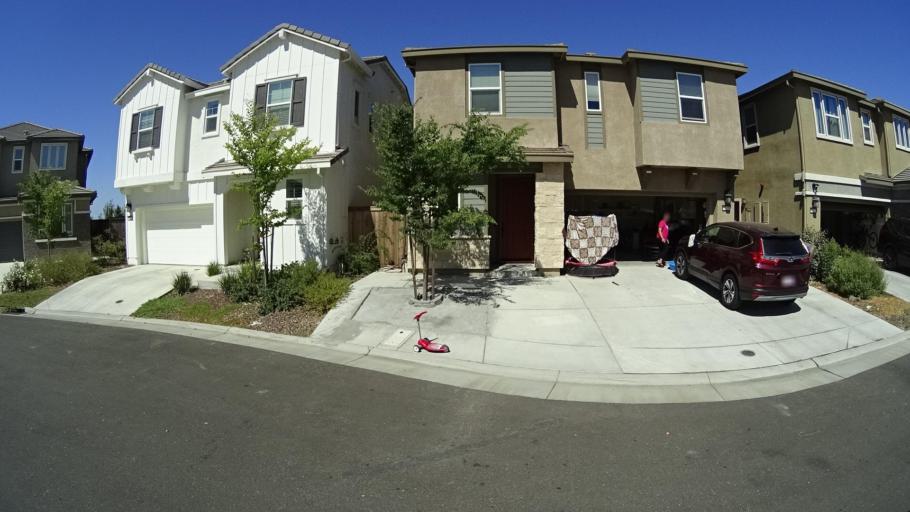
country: US
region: California
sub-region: Placer County
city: Lincoln
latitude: 38.8276
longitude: -121.2902
